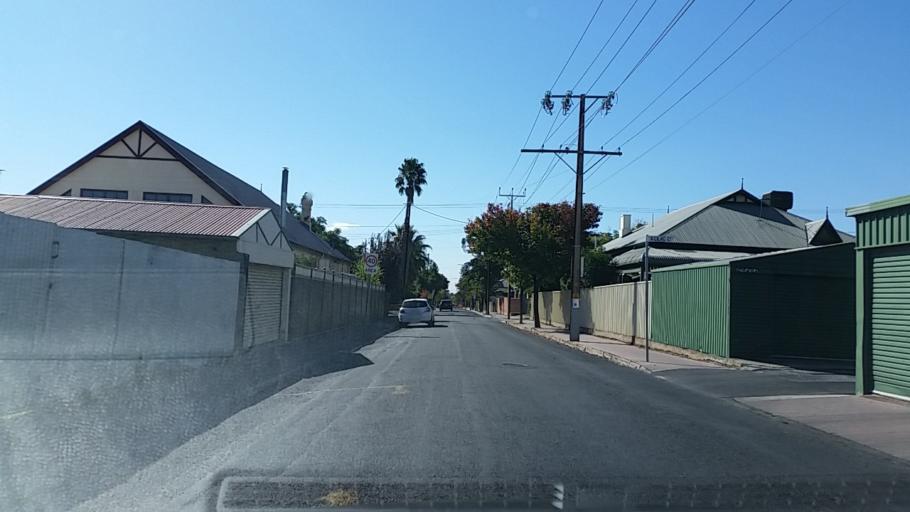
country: AU
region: South Australia
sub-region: Prospect
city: Prospect
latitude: -34.8872
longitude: 138.5895
